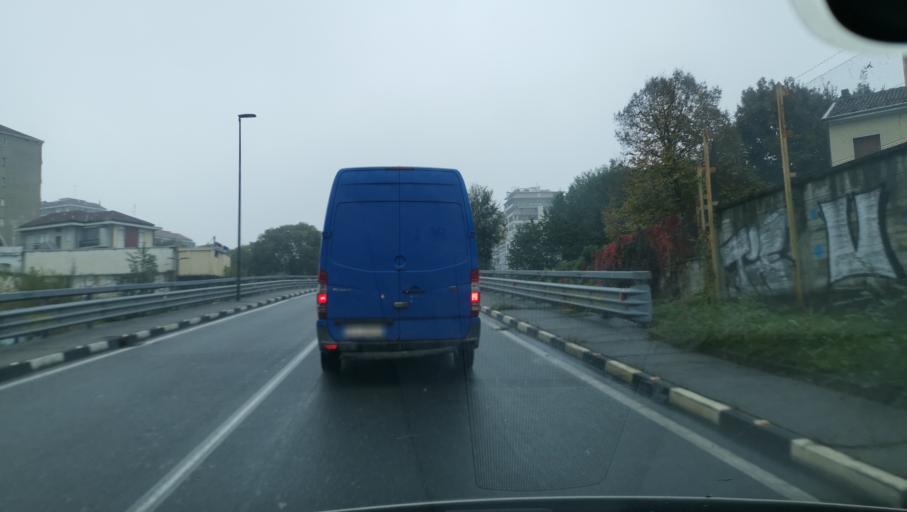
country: IT
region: Piedmont
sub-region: Provincia di Torino
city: Venaria Reale
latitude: 45.0935
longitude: 7.6541
